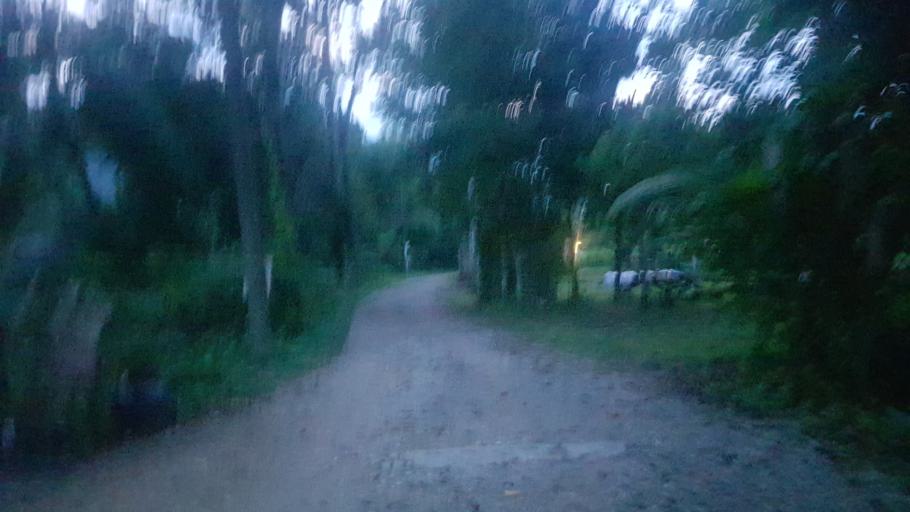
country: TH
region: Phangnga
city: Takua Pa
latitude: 8.9094
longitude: 98.5281
